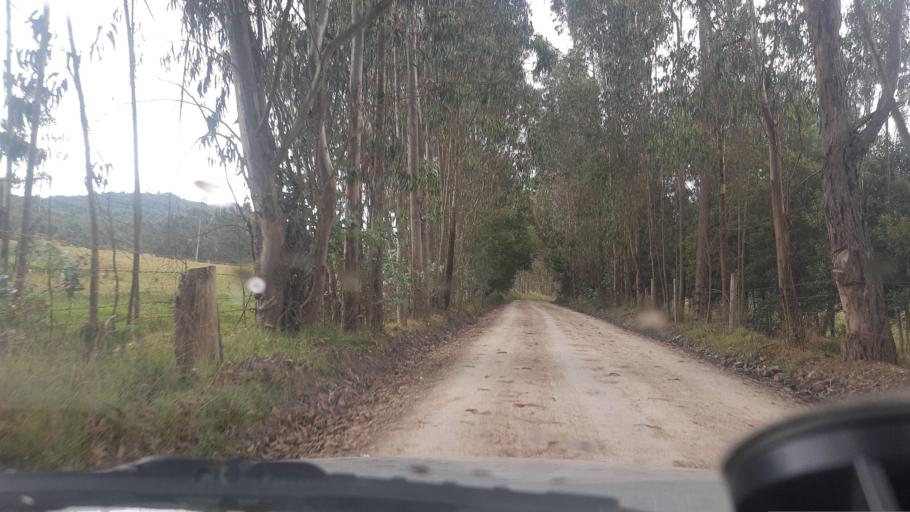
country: CO
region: Cundinamarca
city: Cucunuba
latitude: 5.1882
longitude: -73.7963
